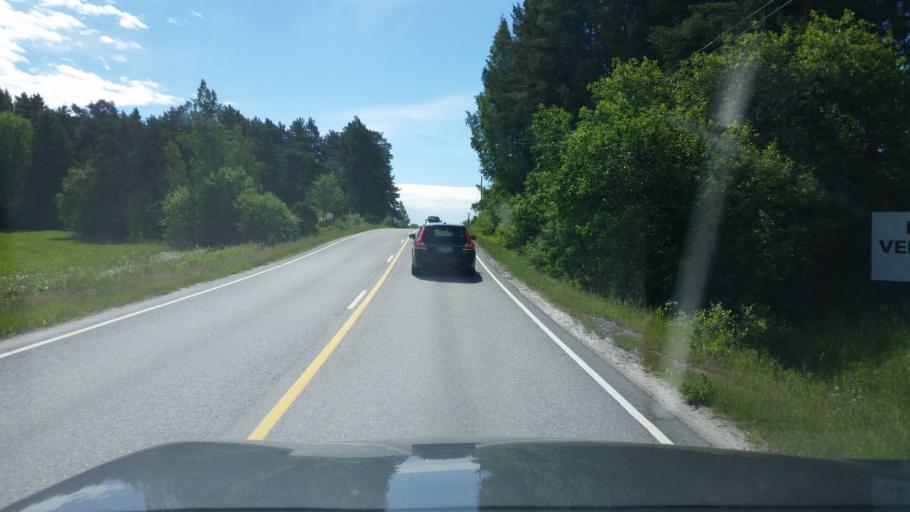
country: FI
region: Varsinais-Suomi
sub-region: Aboland-Turunmaa
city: Laensi-Turunmaa
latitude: 60.2634
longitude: 22.2232
